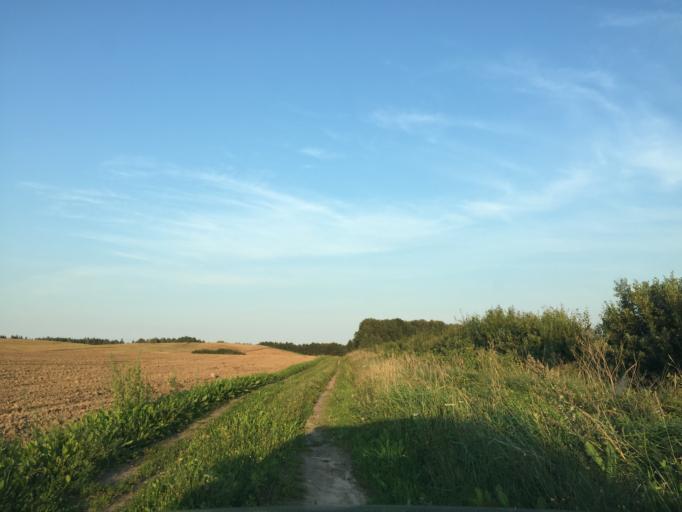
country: LV
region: Limbazu Rajons
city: Limbazi
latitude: 57.5751
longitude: 24.7736
